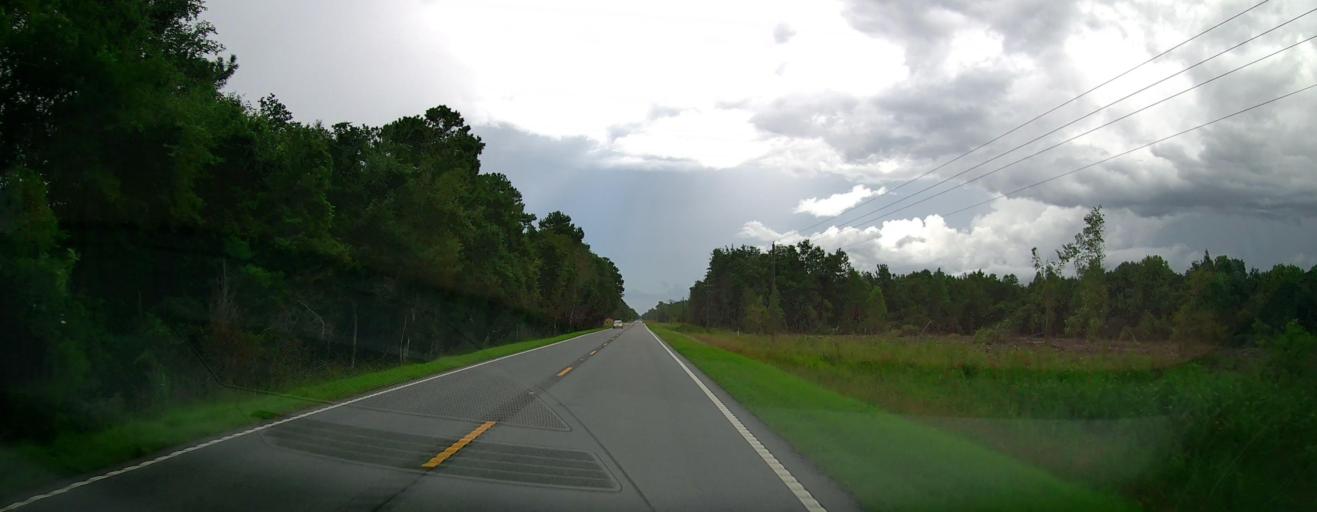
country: US
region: Georgia
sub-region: Pierce County
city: Blackshear
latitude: 31.3692
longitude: -82.0979
